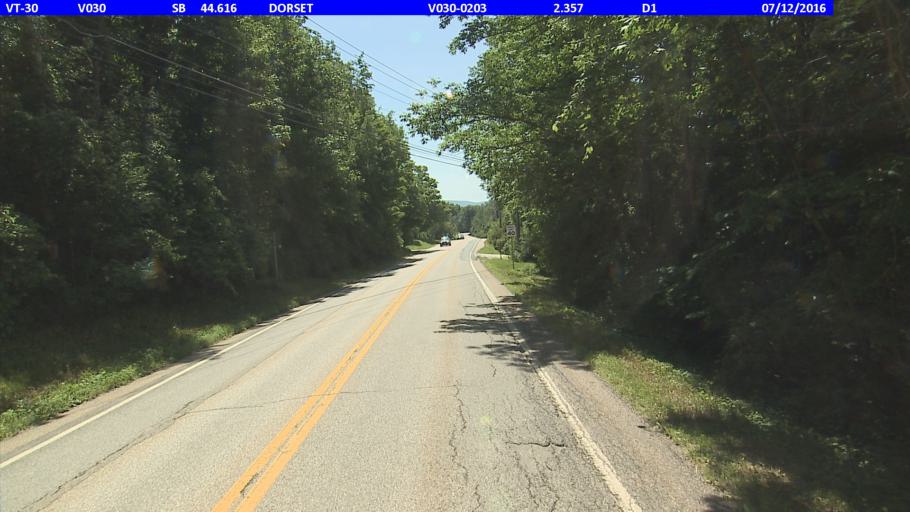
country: US
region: Vermont
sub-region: Bennington County
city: Manchester Center
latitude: 43.2423
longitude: -73.0891
